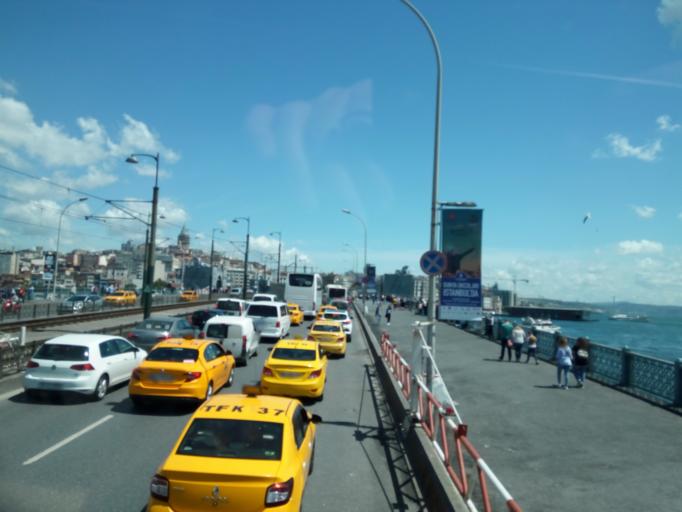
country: TR
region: Istanbul
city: Eminoenue
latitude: 41.0184
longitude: 28.9722
